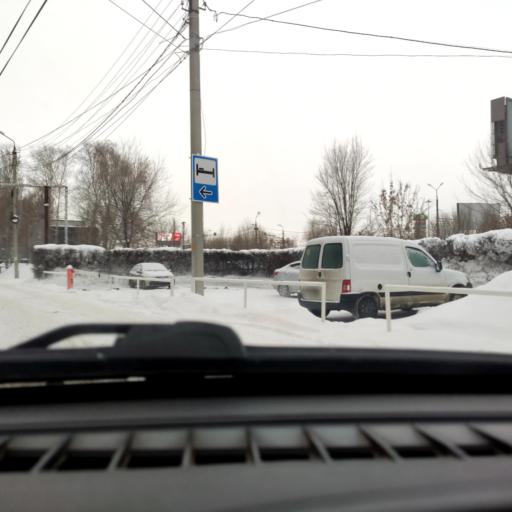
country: RU
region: Samara
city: Tol'yatti
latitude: 53.5382
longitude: 49.3892
